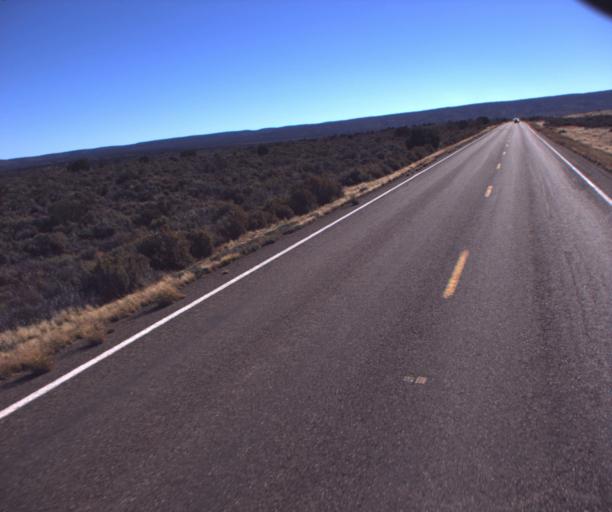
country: US
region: Arizona
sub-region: Coconino County
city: Fredonia
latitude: 36.8696
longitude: -112.3234
